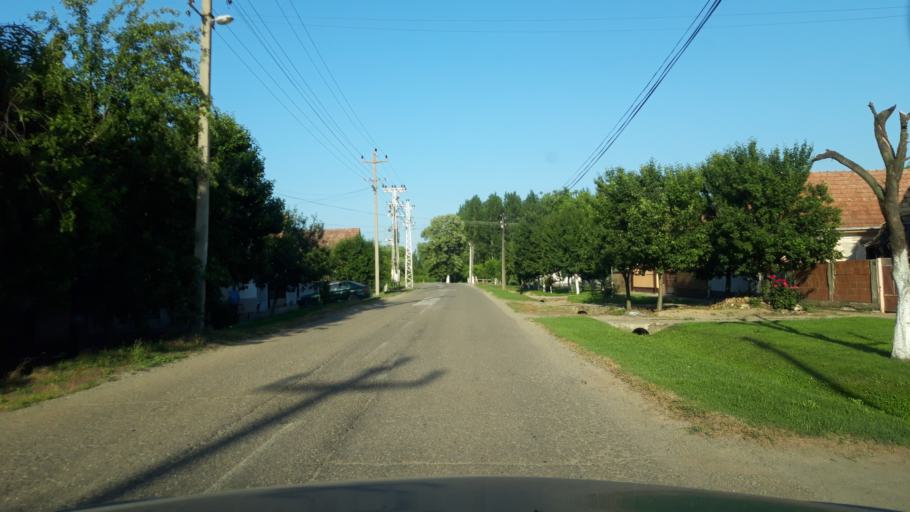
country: HR
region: Vukovarsko-Srijemska
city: Ilok
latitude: 45.1010
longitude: 19.4524
